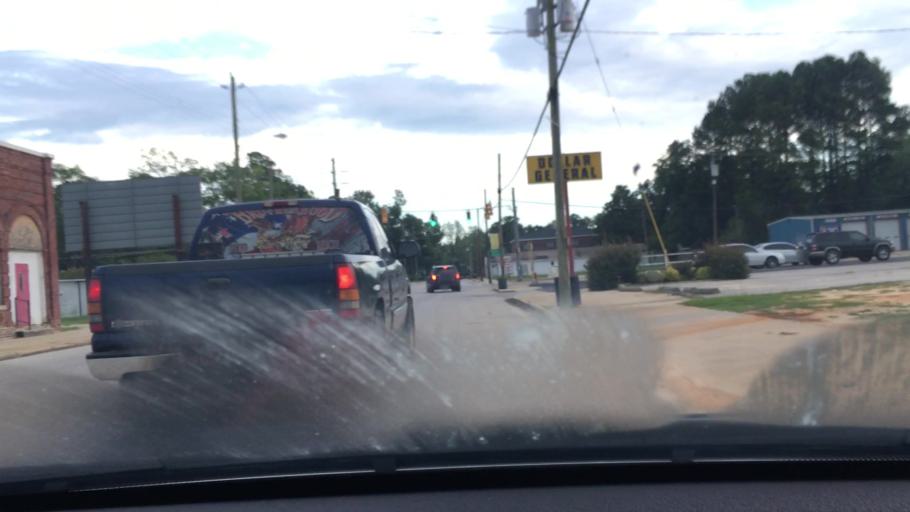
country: US
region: South Carolina
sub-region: Florence County
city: Timmonsville
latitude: 34.1691
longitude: -80.0631
